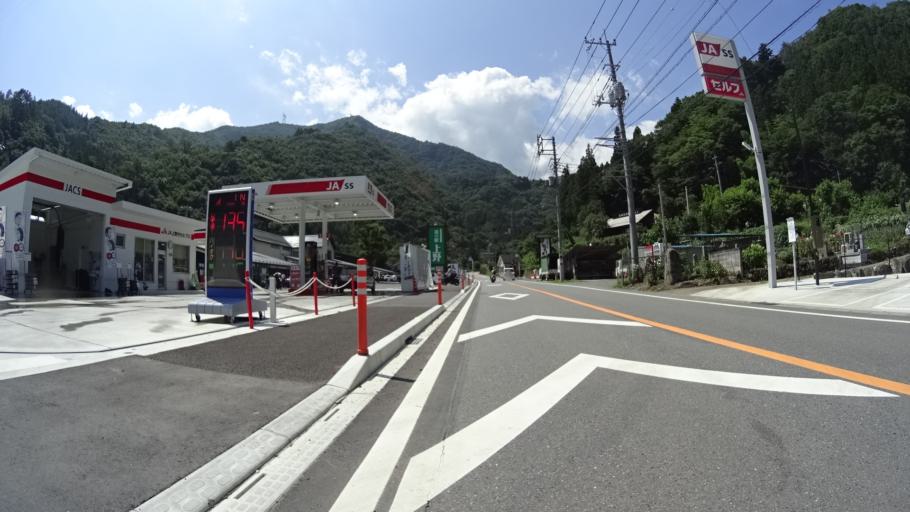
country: JP
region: Gunma
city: Tomioka
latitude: 36.0809
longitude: 138.7839
